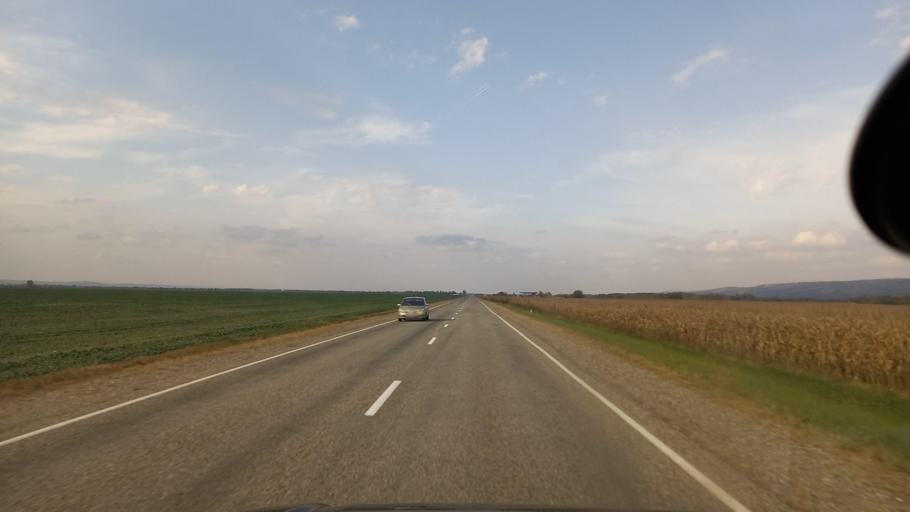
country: RU
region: Krasnodarskiy
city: Perepravnaya
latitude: 44.3275
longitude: 40.8497
